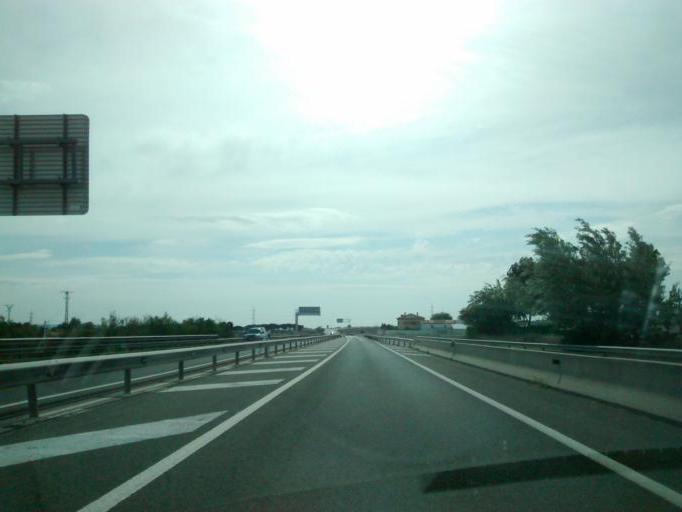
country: ES
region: Aragon
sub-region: Provincia de Zaragoza
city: El Burgo de Ebro
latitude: 41.5804
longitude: -0.7657
